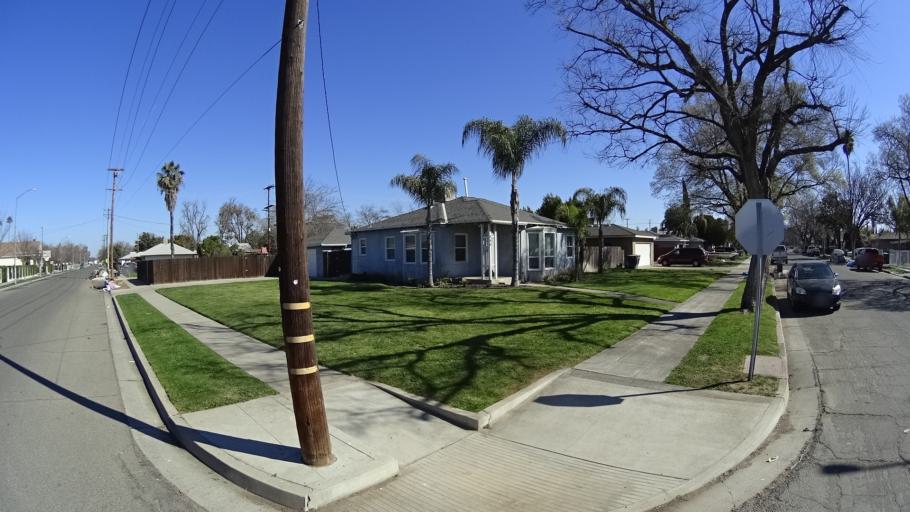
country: US
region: California
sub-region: Fresno County
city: West Park
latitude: 36.7222
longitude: -119.8176
